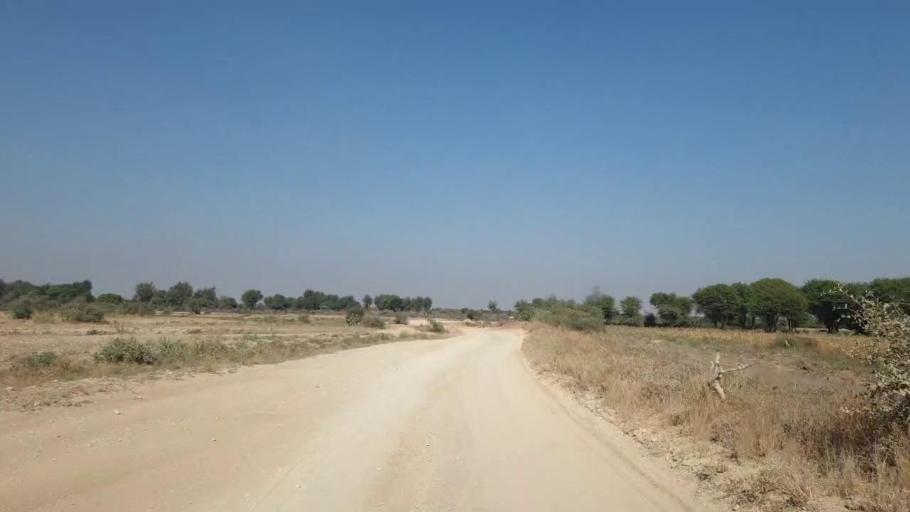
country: PK
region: Sindh
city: Jamshoro
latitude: 25.2993
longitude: 67.8151
